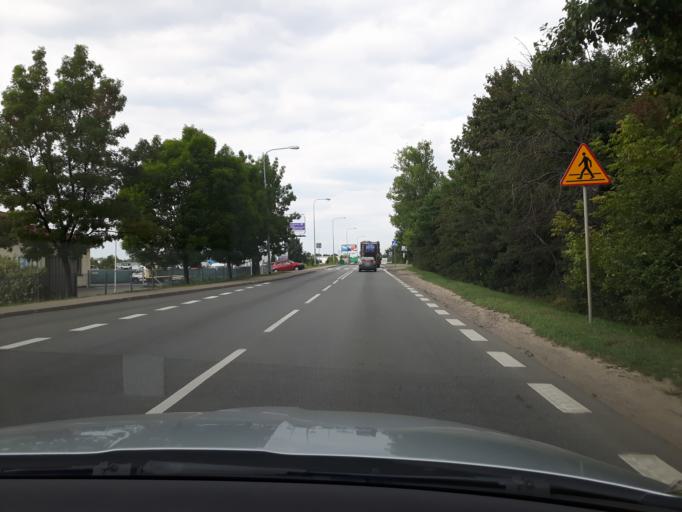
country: PL
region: Masovian Voivodeship
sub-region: Warszawa
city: Targowek
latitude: 52.3330
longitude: 21.0301
